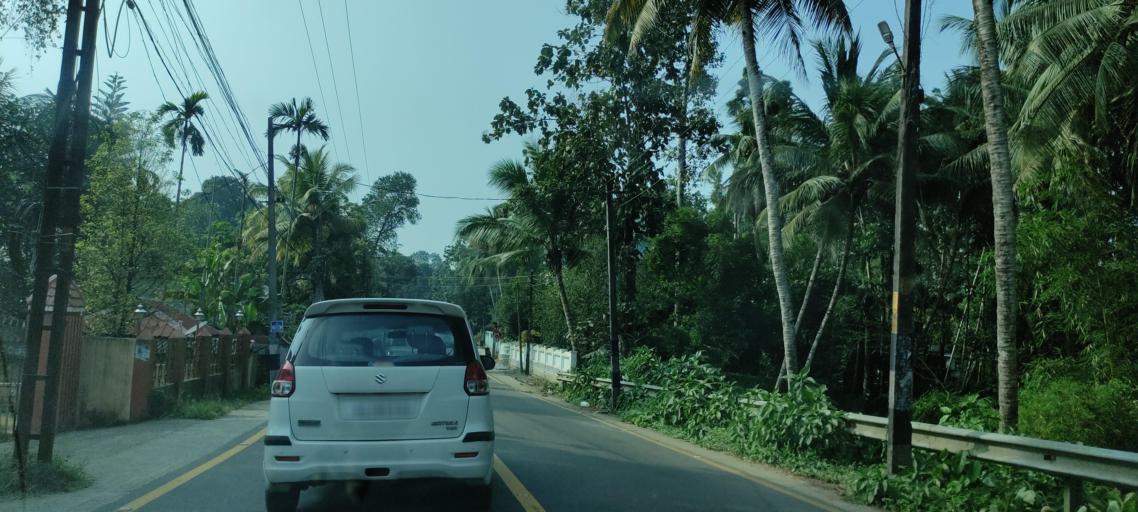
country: IN
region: Kerala
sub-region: Pattanamtitta
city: Tiruvalla
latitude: 9.3679
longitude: 76.5312
